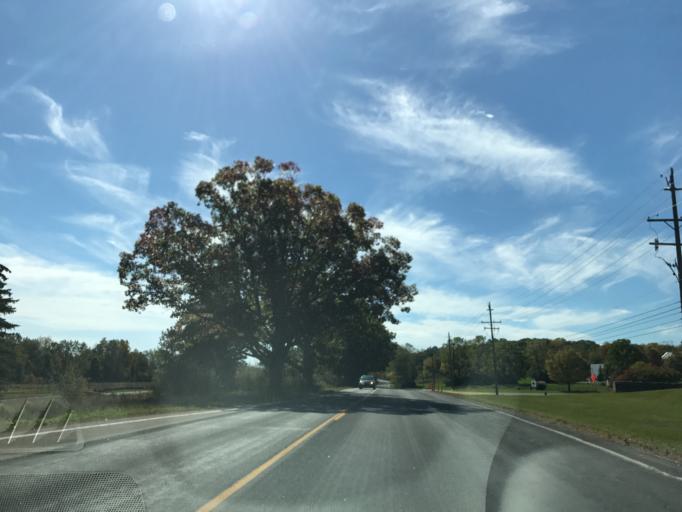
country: US
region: Michigan
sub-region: Washtenaw County
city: Ann Arbor
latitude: 42.2995
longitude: -83.6663
